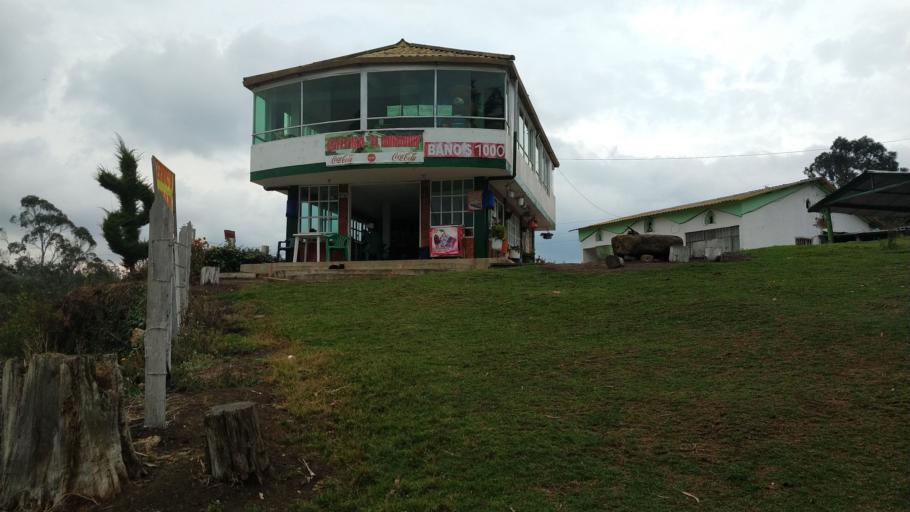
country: CO
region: Boyaca
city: Samaca
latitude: 5.4498
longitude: -73.4296
